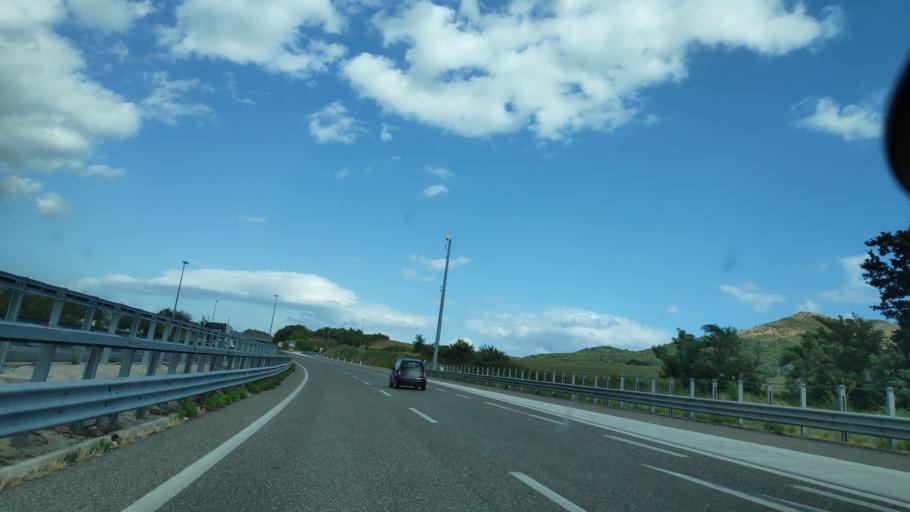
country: IT
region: Campania
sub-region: Provincia di Salerno
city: Palomonte
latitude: 40.6104
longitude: 15.2870
